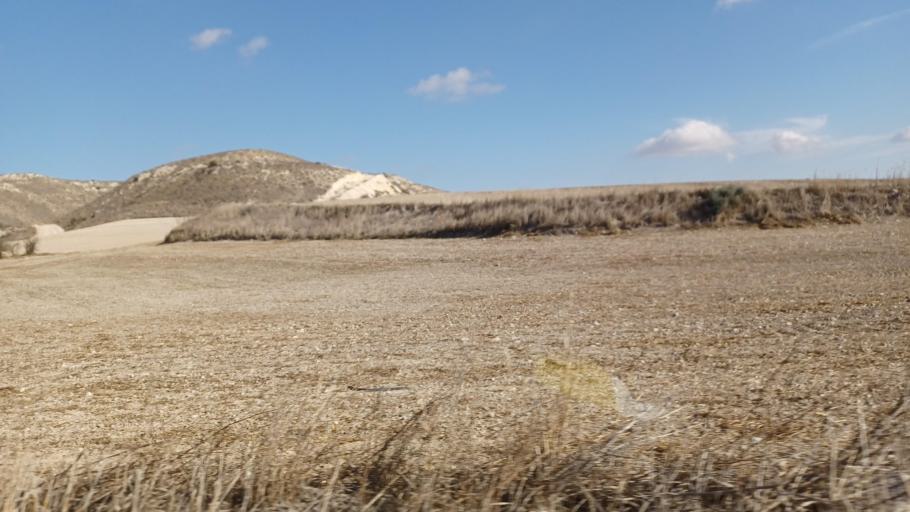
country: CY
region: Larnaka
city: Troulloi
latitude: 35.0275
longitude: 33.5813
